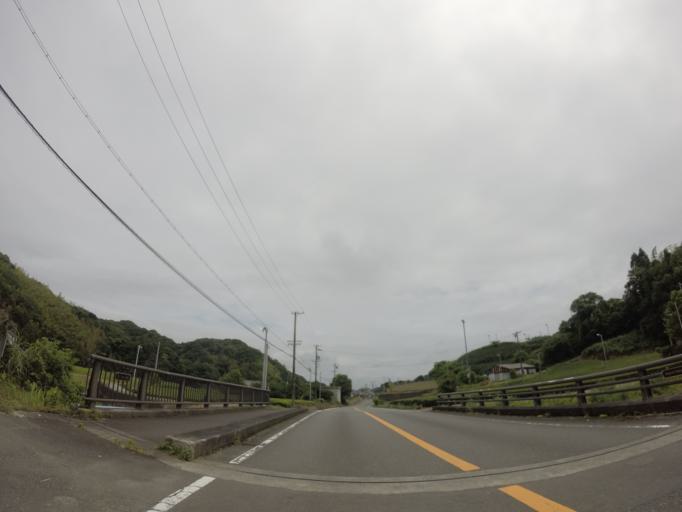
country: JP
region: Shizuoka
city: Kanaya
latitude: 34.7864
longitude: 138.1534
